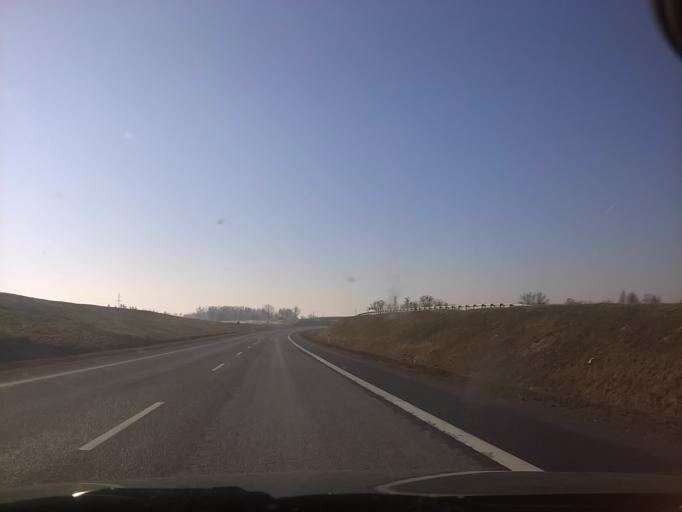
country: PL
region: Warmian-Masurian Voivodeship
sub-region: Powiat olsztynski
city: Czerwonka
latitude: 53.8276
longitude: 20.8707
